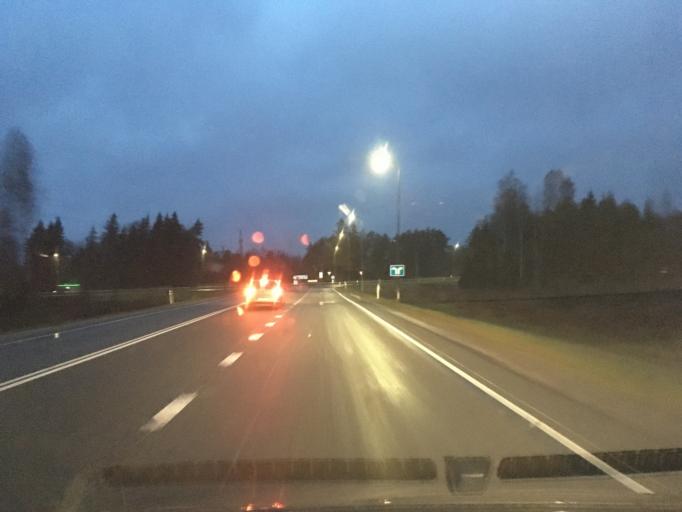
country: EE
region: Harju
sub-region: Nissi vald
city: Turba
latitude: 58.9923
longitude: 24.0585
